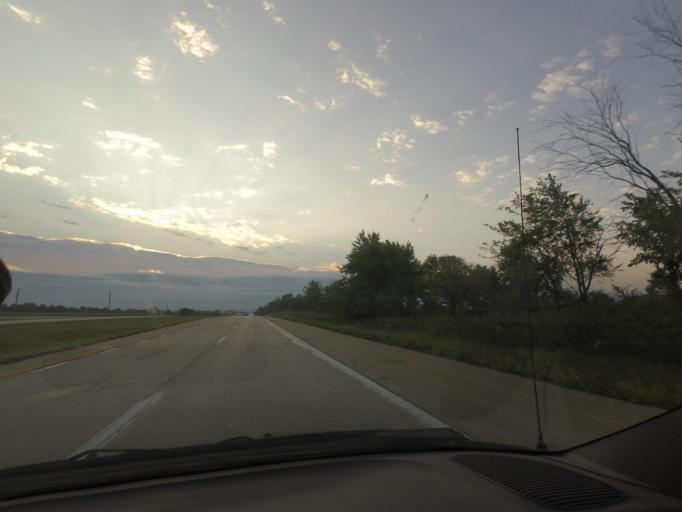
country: US
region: Missouri
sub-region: Shelby County
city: Shelbina
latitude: 39.7397
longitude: -92.2376
